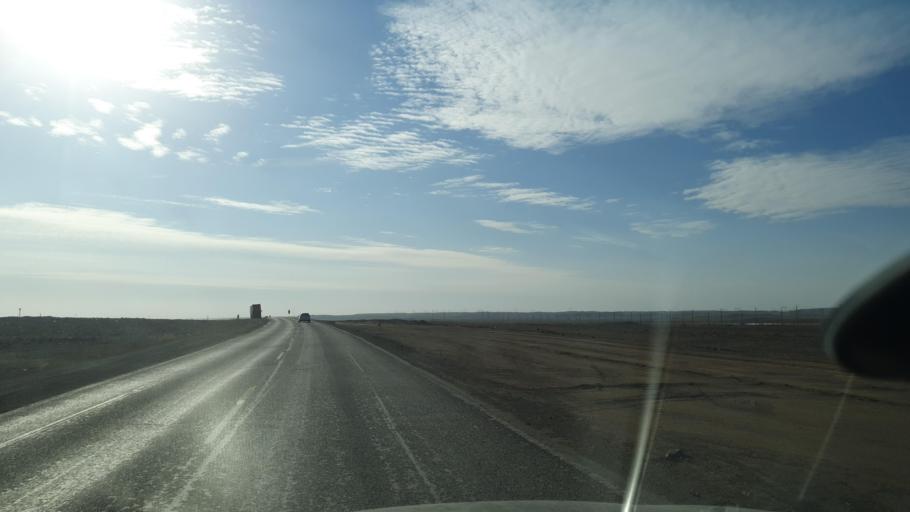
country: KZ
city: Priozersk
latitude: 45.8676
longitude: 73.4726
